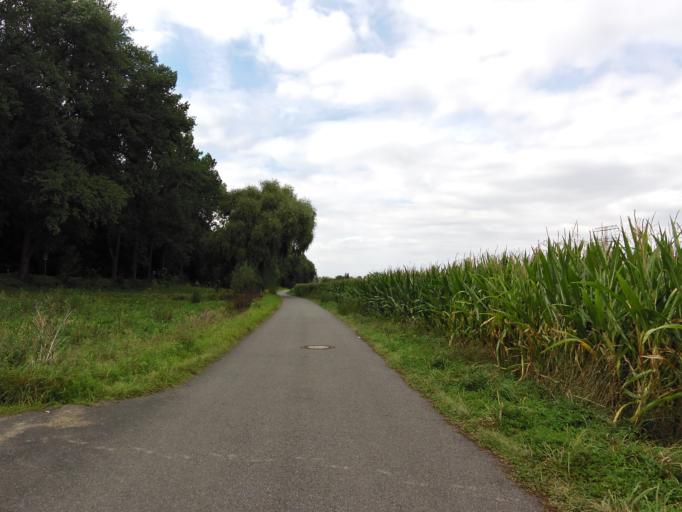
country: DE
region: Saxony
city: Coswig
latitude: 51.1055
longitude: 13.5772
